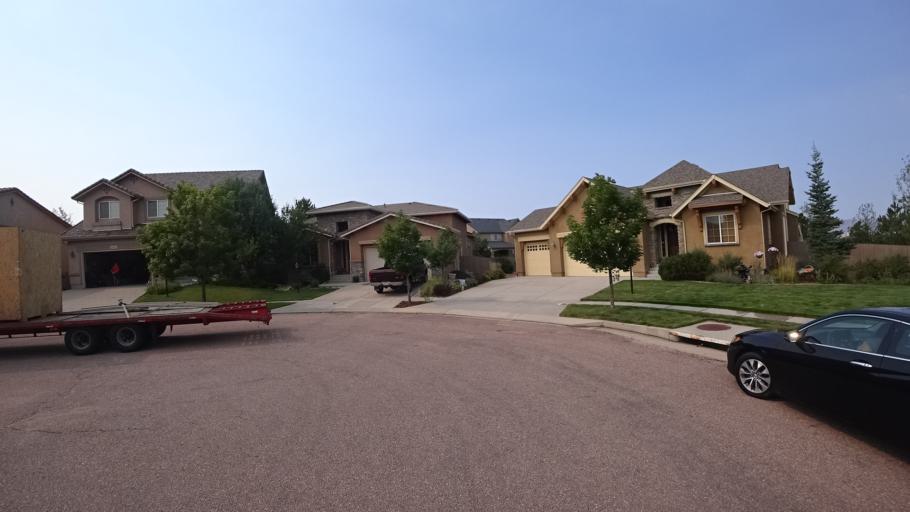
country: US
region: Colorado
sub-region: El Paso County
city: Black Forest
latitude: 38.9704
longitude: -104.7375
